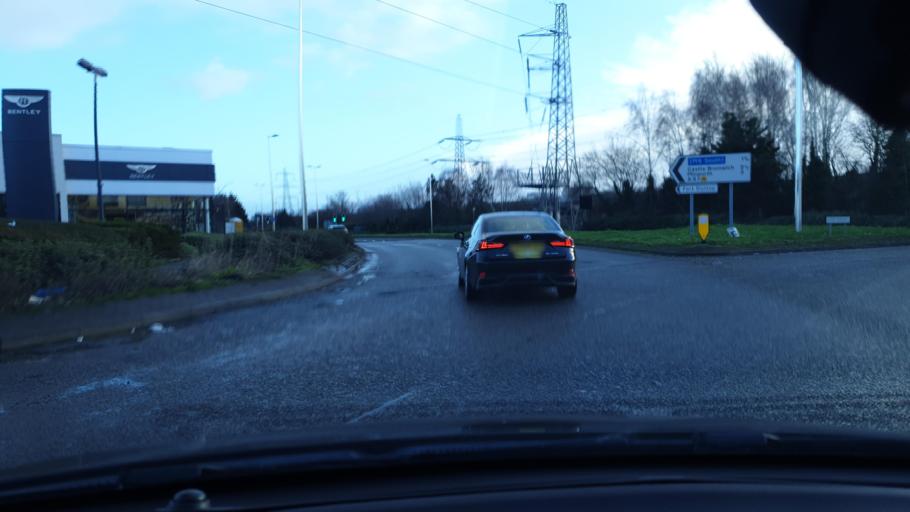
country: GB
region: England
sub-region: City and Borough of Birmingham
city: Acocks Green
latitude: 52.5081
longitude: -1.8194
